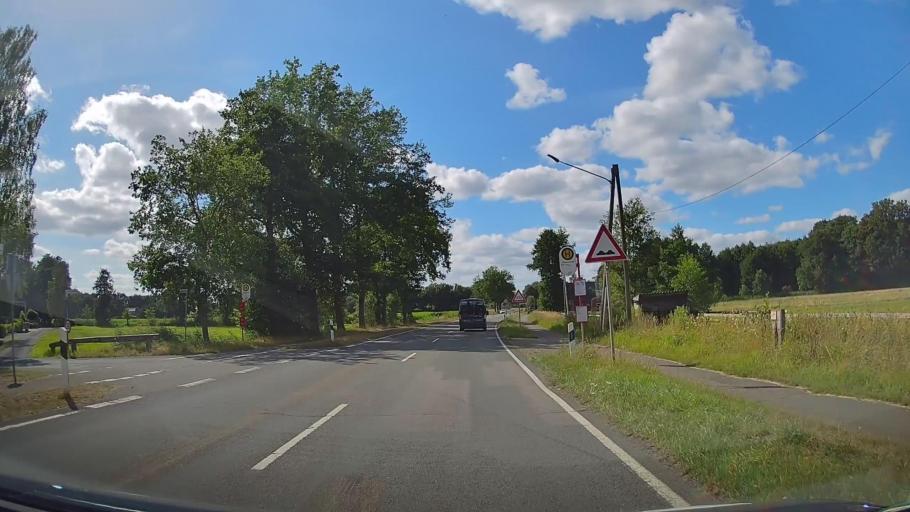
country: DE
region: Lower Saxony
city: Alfhausen
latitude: 52.5000
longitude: 7.9730
